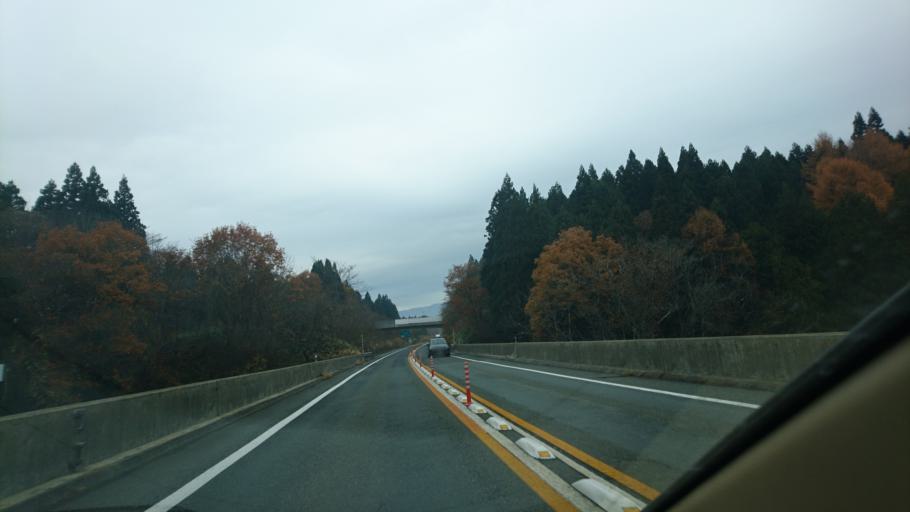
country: JP
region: Iwate
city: Kitakami
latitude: 39.2843
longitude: 140.9974
